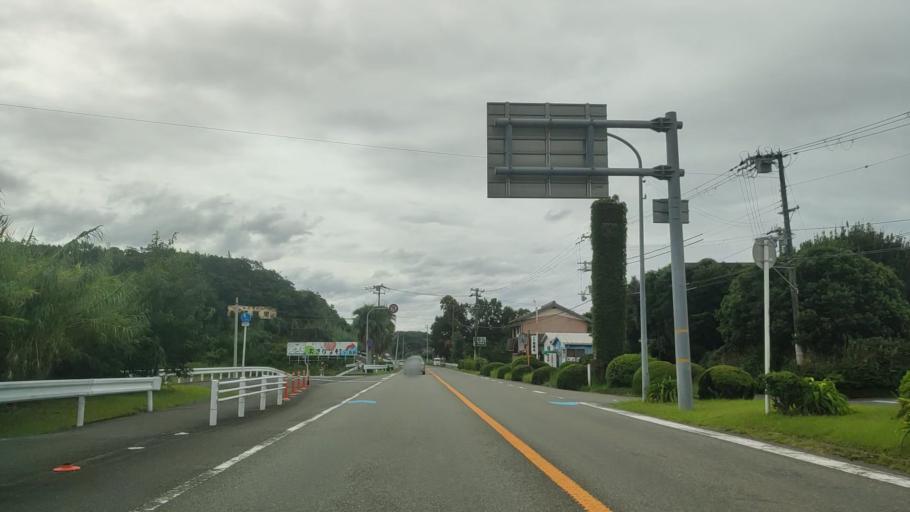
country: JP
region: Wakayama
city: Tanabe
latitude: 33.6988
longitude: 135.3886
